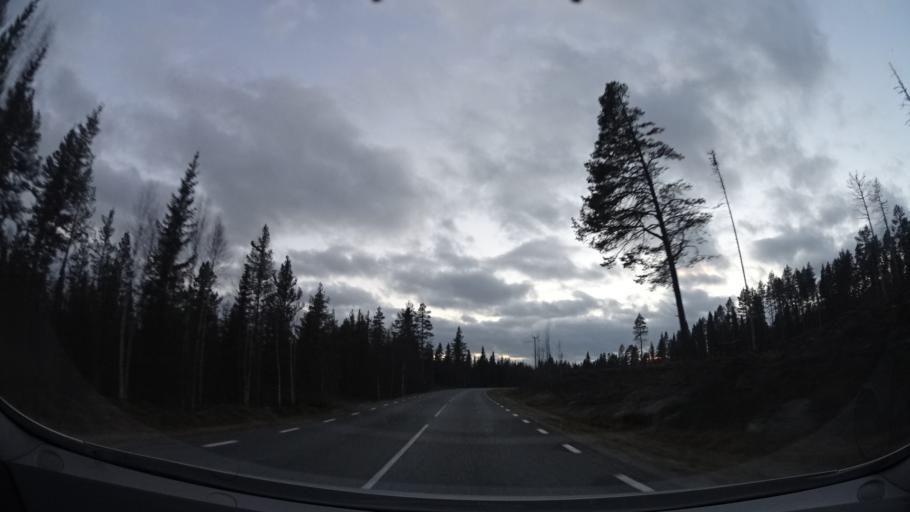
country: SE
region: Vaesterbotten
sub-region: Asele Kommun
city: Insjon
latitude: 64.3251
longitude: 17.7224
